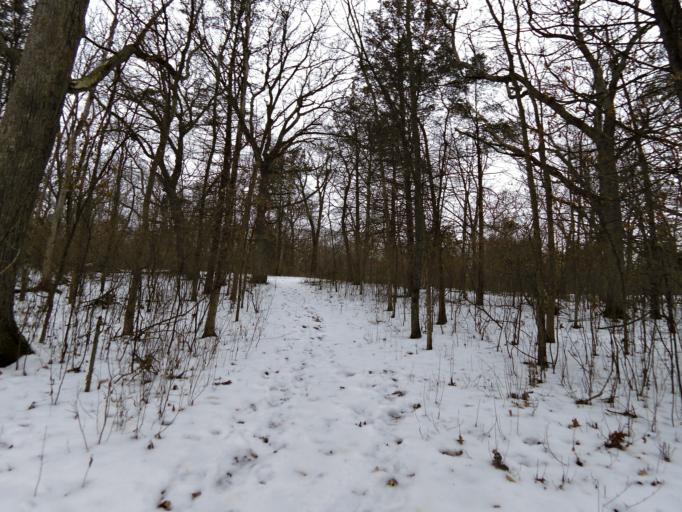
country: US
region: Wisconsin
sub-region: Pierce County
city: Prescott
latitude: 44.8020
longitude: -92.7879
